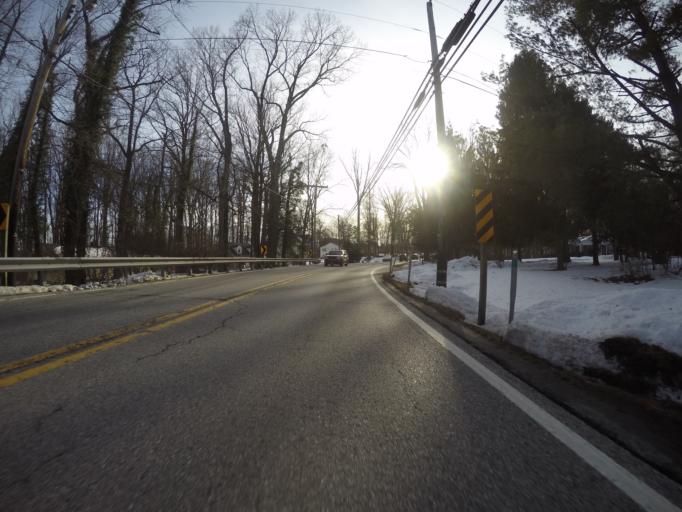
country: US
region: Maryland
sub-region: Baltimore County
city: Hunt Valley
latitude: 39.5106
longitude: -76.5619
